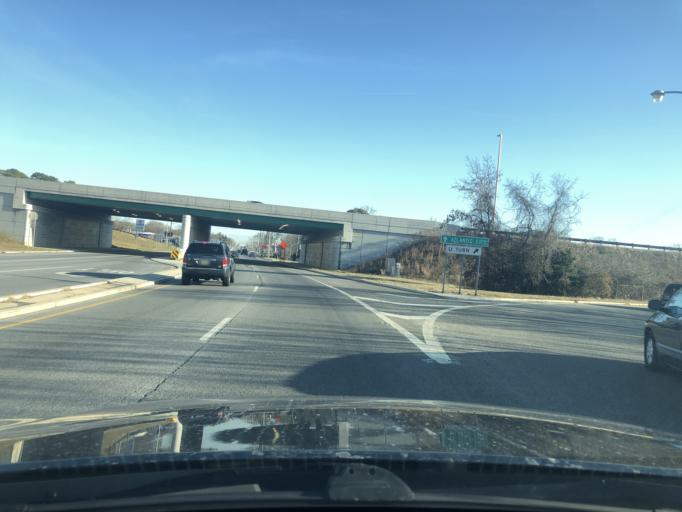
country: US
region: New Jersey
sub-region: Atlantic County
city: Northfield
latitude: 39.4004
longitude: -74.5609
